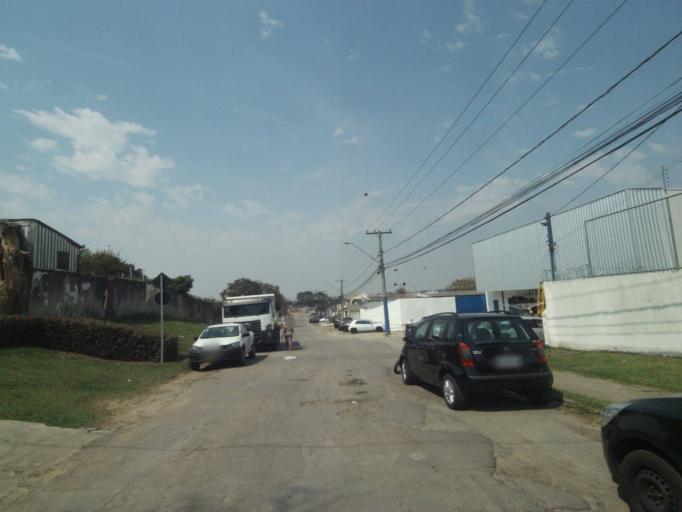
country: BR
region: Parana
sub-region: Curitiba
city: Curitiba
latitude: -25.4658
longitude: -49.2616
